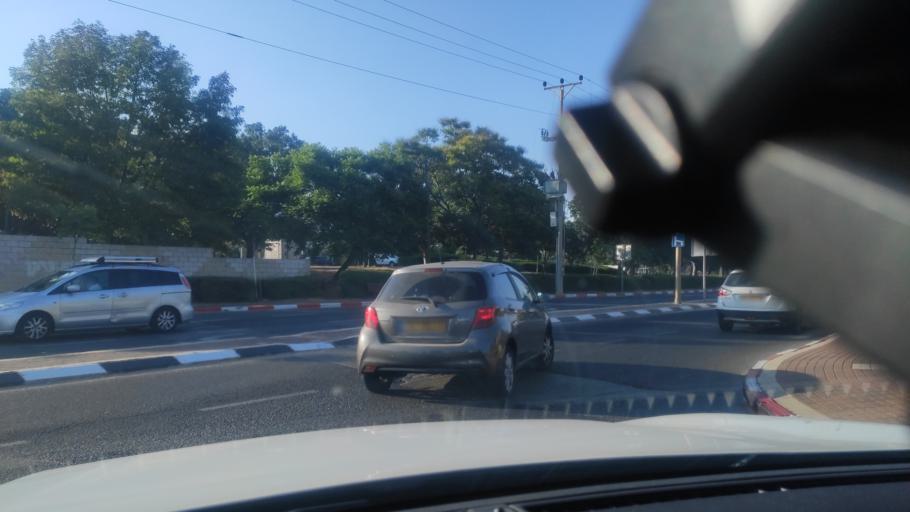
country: IL
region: Central District
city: Kfar Saba
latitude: 32.1767
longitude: 34.9350
